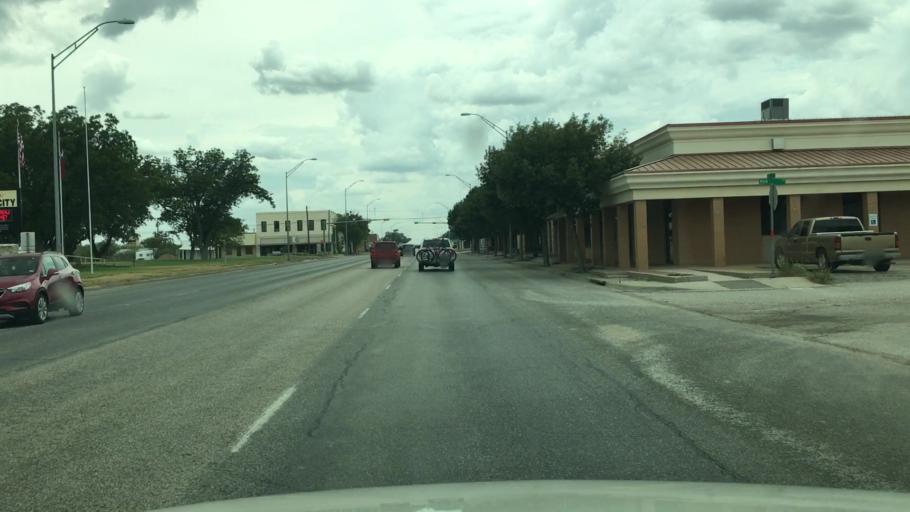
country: US
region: Texas
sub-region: Sterling County
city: Sterling City
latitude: 31.8365
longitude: -100.9868
